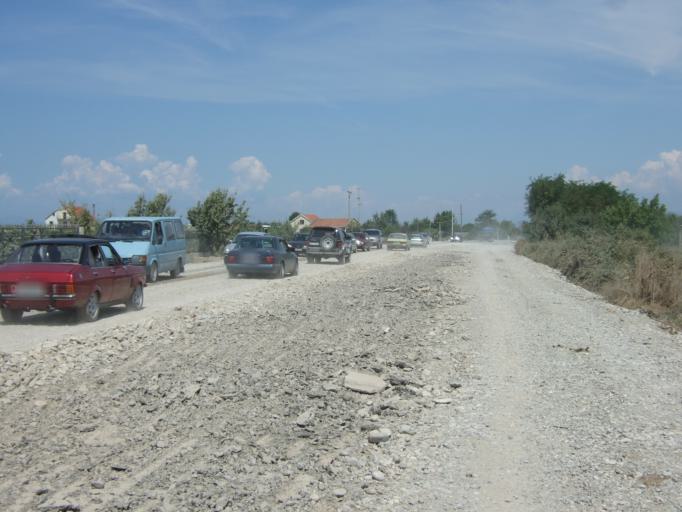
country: AL
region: Shkoder
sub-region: Rrethi i Shkodres
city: Shkoder
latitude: 42.1139
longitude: 19.4988
